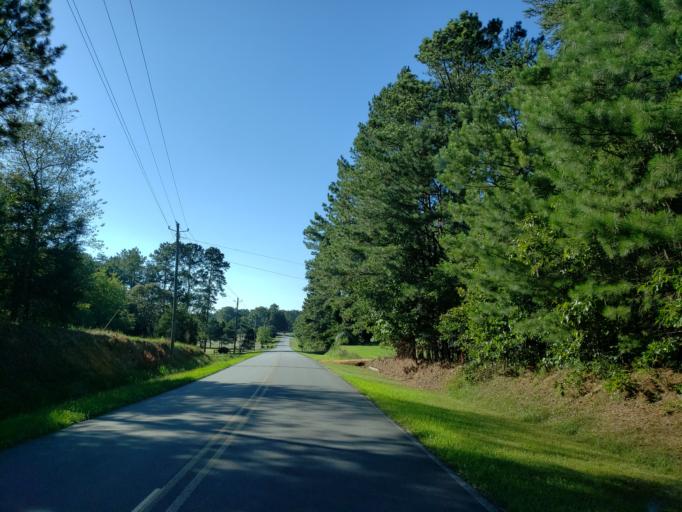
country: US
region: Georgia
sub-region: Bartow County
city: Euharlee
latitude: 34.1184
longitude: -85.0115
